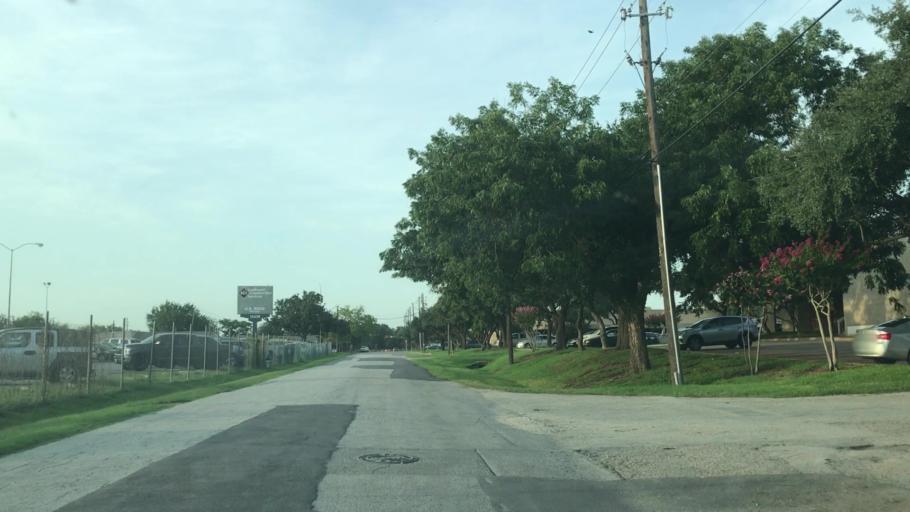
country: US
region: Texas
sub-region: Dallas County
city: Farmers Branch
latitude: 32.8985
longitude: -96.9079
